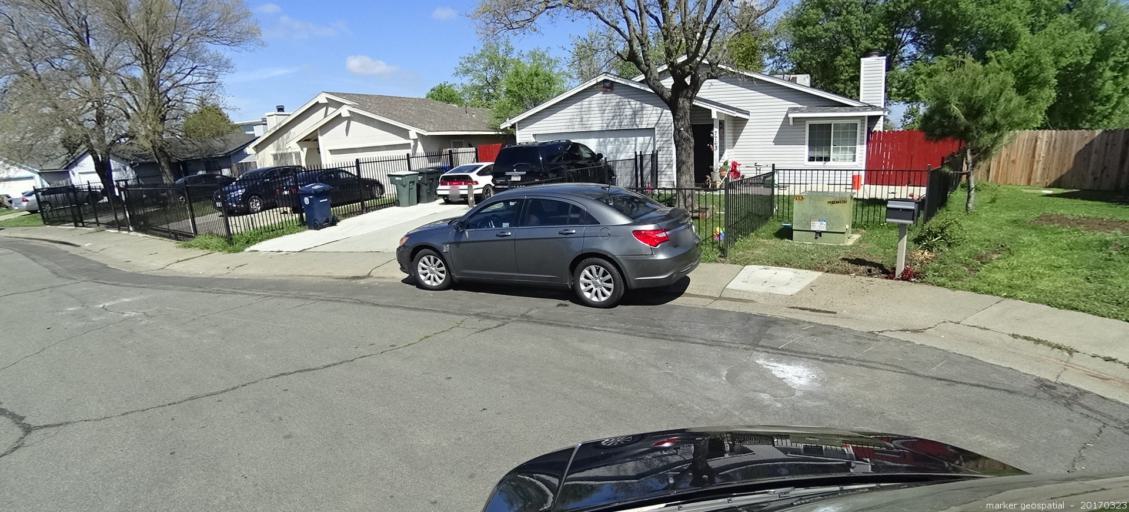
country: US
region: California
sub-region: Sacramento County
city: Florin
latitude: 38.5122
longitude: -121.4132
